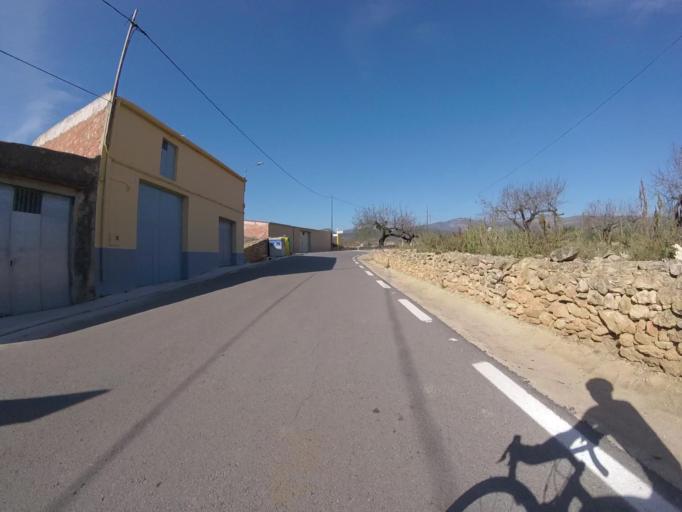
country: ES
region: Valencia
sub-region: Provincia de Castello
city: Sarratella
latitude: 40.2635
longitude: 0.0687
